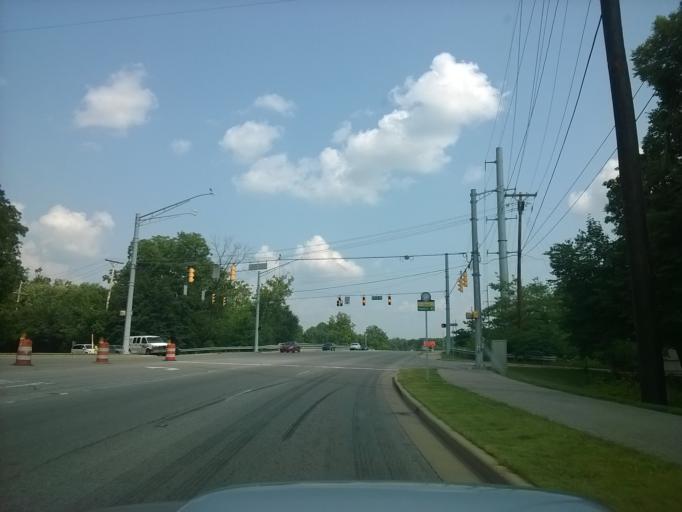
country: US
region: Indiana
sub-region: Hamilton County
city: Fishers
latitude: 39.9566
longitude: -86.0667
